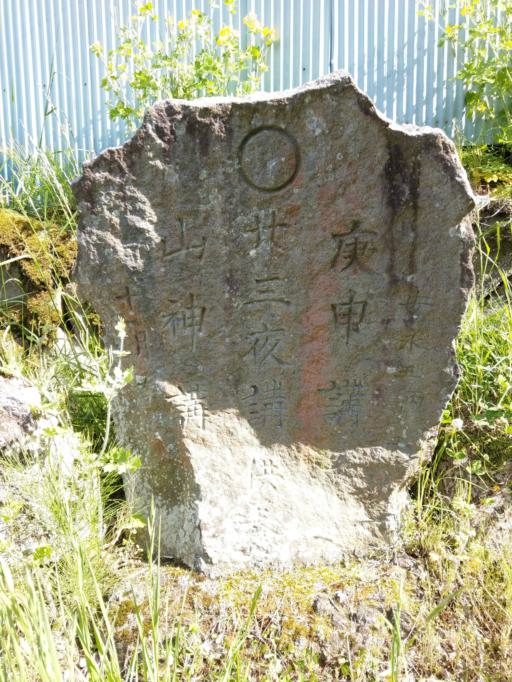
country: JP
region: Nagano
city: Komoro
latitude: 36.3199
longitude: 138.4112
